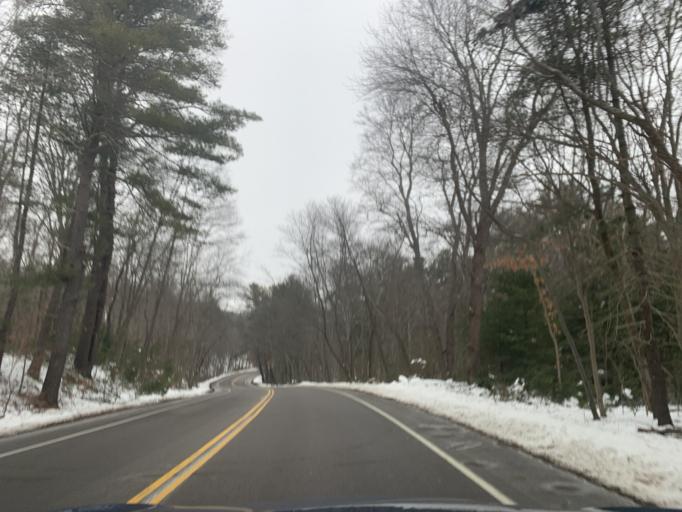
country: US
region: Massachusetts
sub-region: Norfolk County
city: Milton
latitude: 42.2285
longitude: -71.0941
